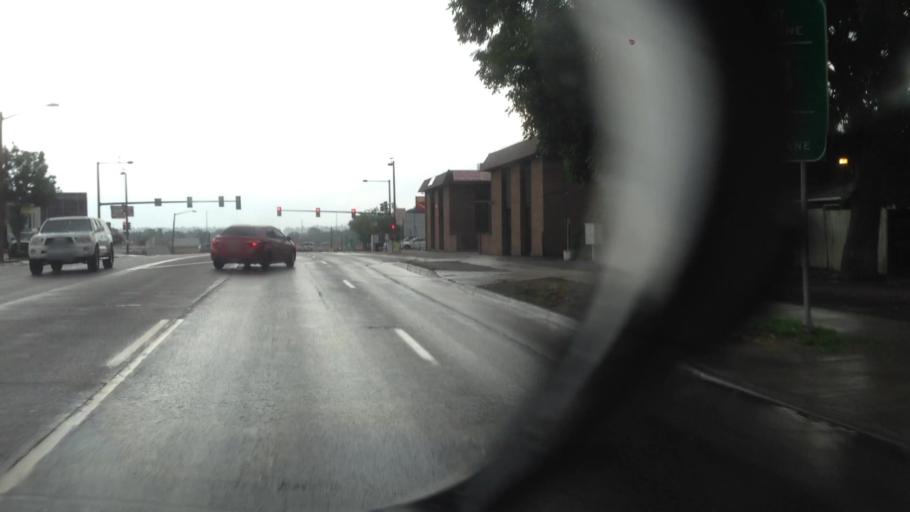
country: US
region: Colorado
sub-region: Jefferson County
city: Edgewater
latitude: 39.7229
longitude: -105.0532
